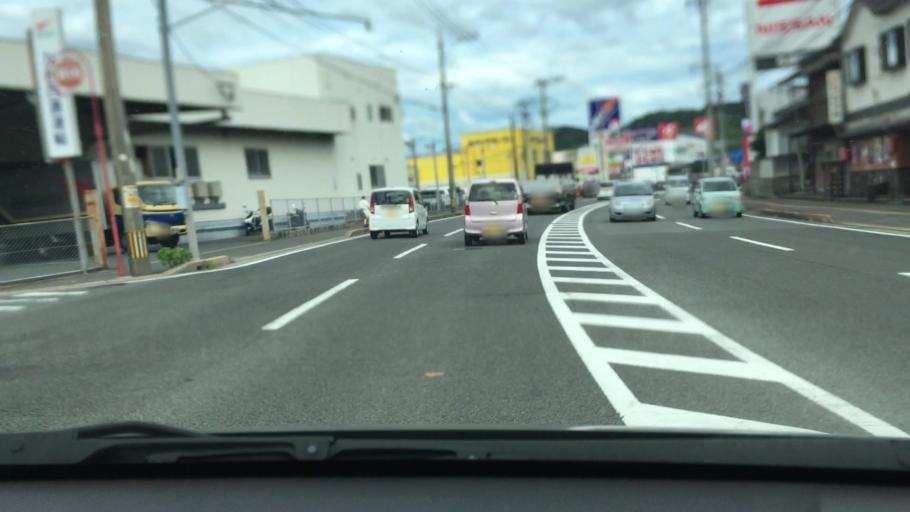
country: JP
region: Nagasaki
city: Togitsu
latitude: 32.8337
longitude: 129.8431
